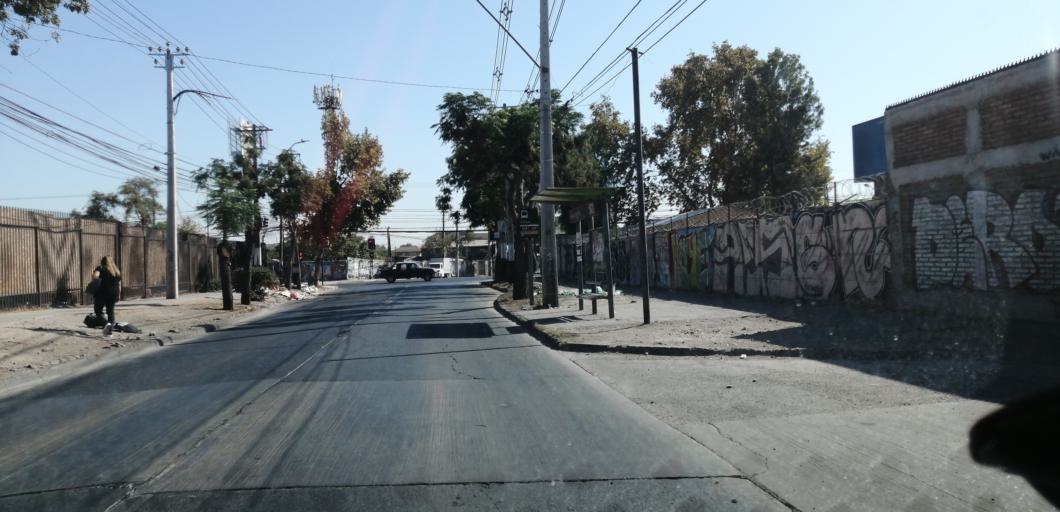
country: CL
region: Santiago Metropolitan
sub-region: Provincia de Santiago
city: Lo Prado
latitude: -33.4436
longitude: -70.7688
